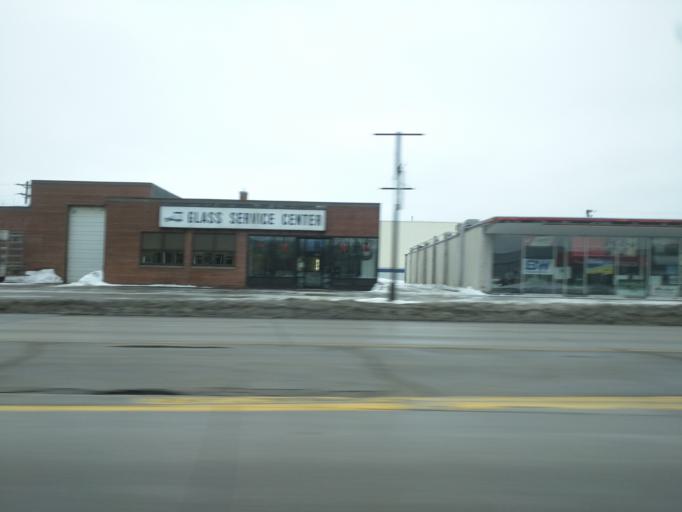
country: US
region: Wisconsin
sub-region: La Crosse County
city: North La Crosse
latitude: 43.8244
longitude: -91.2493
